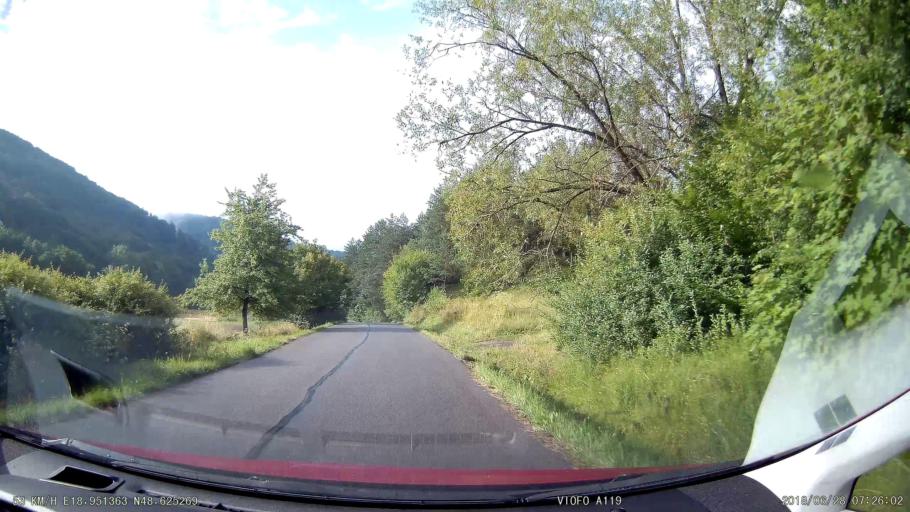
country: SK
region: Banskobystricky
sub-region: Okres Ziar nad Hronom
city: Kremnica
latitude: 48.6250
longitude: 18.9514
